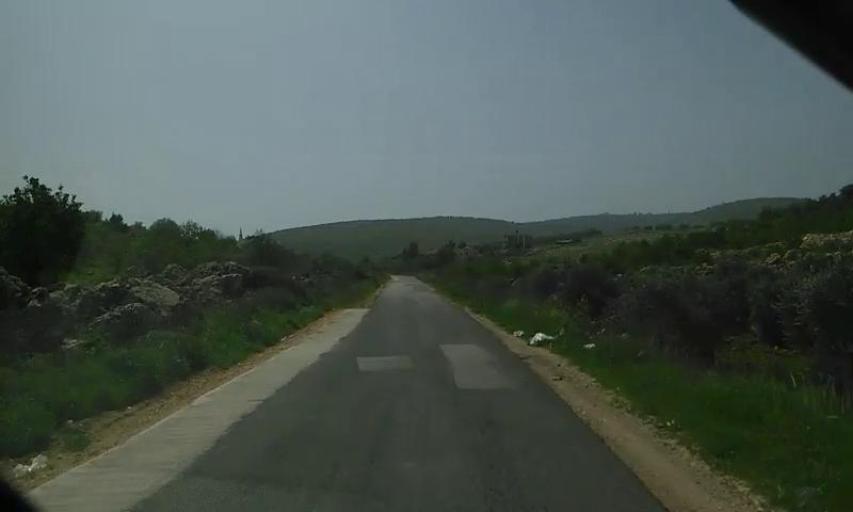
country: PS
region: West Bank
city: At Taybah
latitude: 32.5070
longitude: 35.2012
